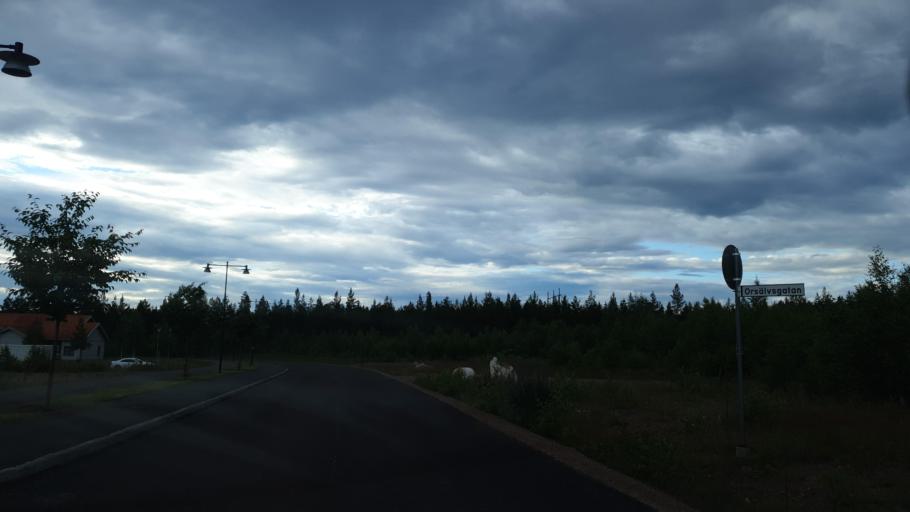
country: SE
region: Dalarna
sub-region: Mora Kommun
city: Mora
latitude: 61.0209
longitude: 14.5867
